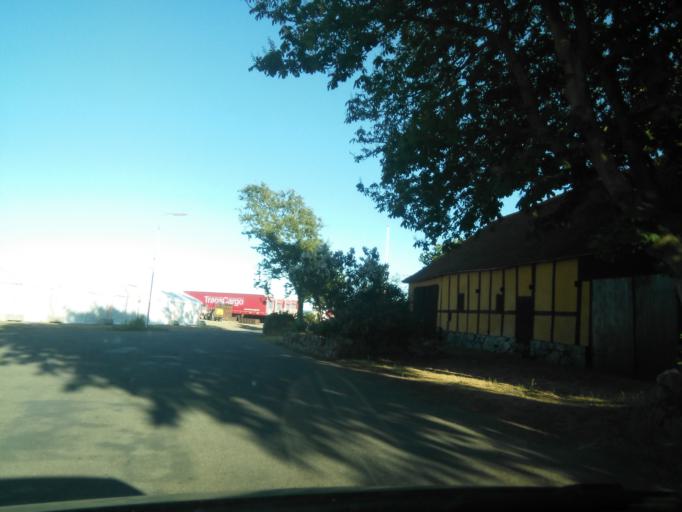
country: DK
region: Capital Region
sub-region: Bornholm Kommune
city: Ronne
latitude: 55.2771
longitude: 14.8041
